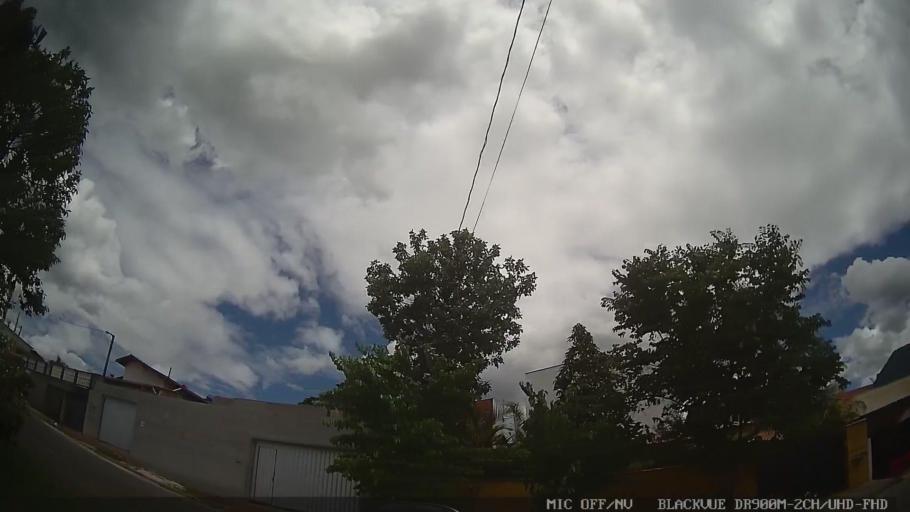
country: BR
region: Sao Paulo
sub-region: Jaguariuna
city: Jaguariuna
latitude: -22.7063
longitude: -46.9633
